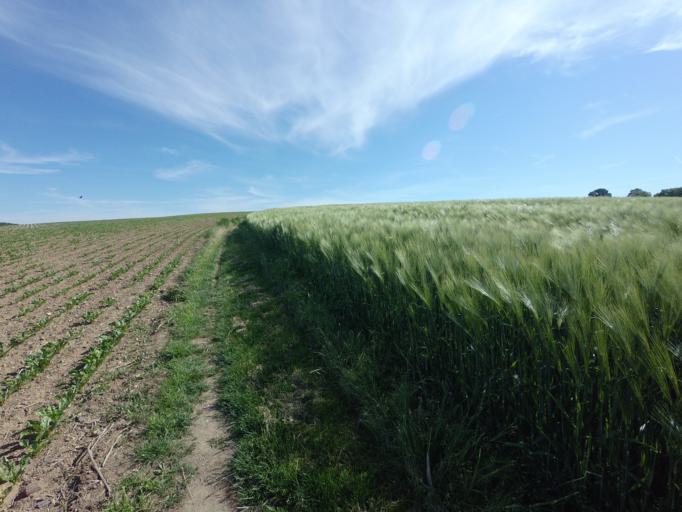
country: NL
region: Limburg
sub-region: Gemeente Voerendaal
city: Ubachsberg
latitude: 50.8144
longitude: 5.9284
